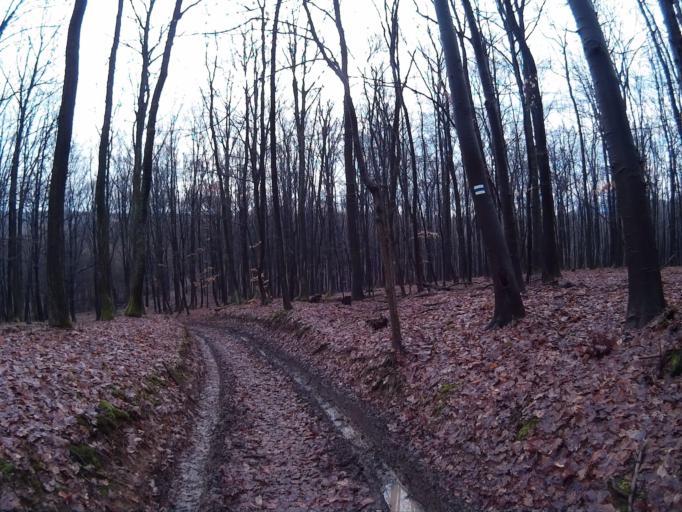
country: HU
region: Borsod-Abauj-Zemplen
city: Satoraljaujhely
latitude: 48.4181
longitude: 21.5807
